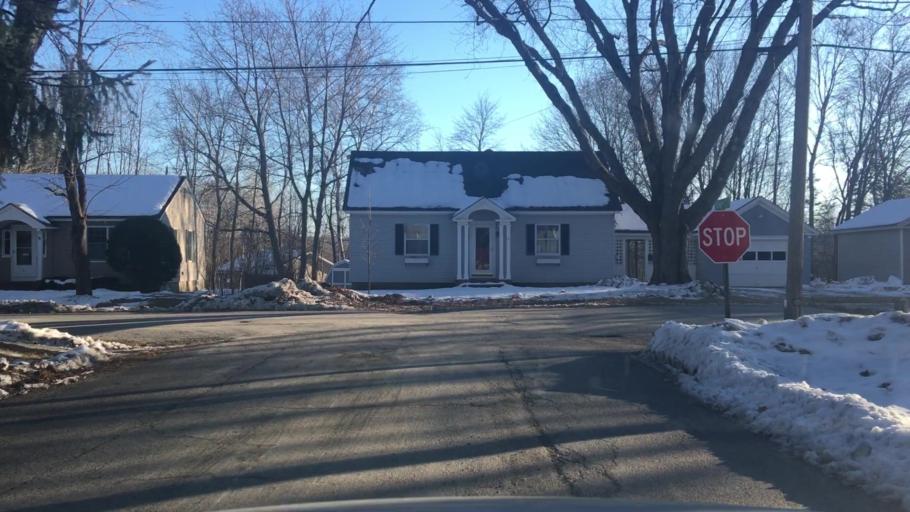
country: US
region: Maine
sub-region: Somerset County
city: Skowhegan
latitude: 44.7736
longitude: -69.7209
